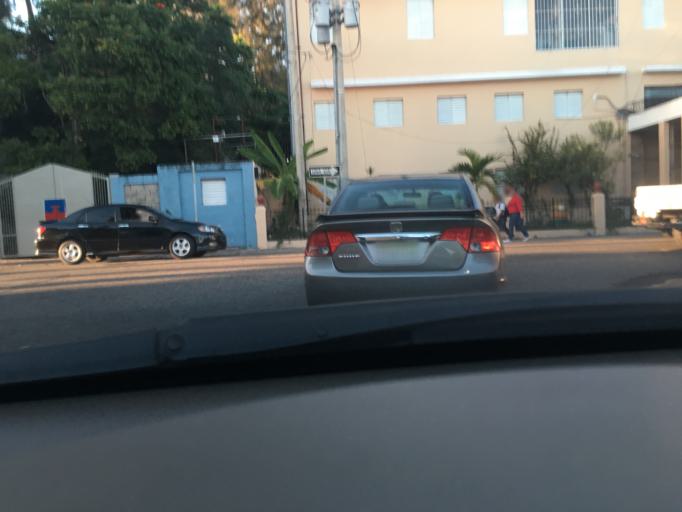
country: DO
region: Nacional
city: San Carlos
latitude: 18.4775
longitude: -69.9012
